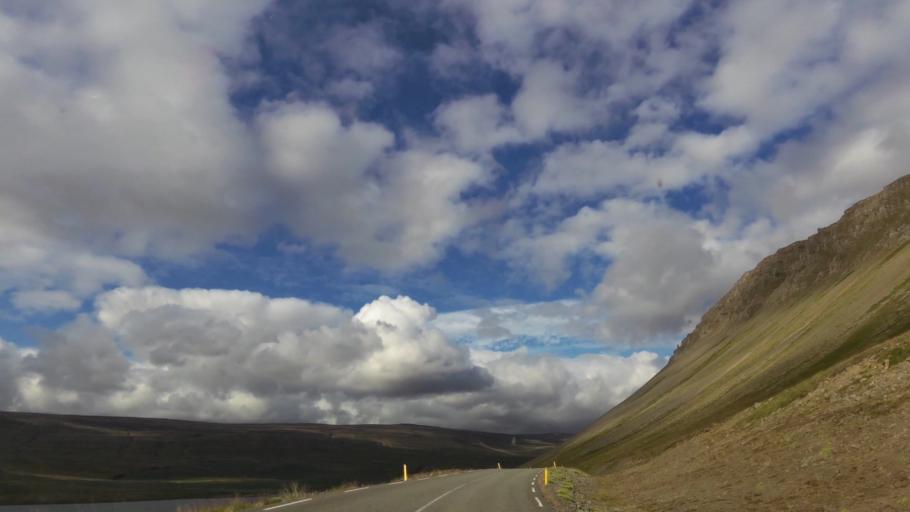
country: IS
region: West
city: Olafsvik
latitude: 65.5215
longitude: -23.8324
